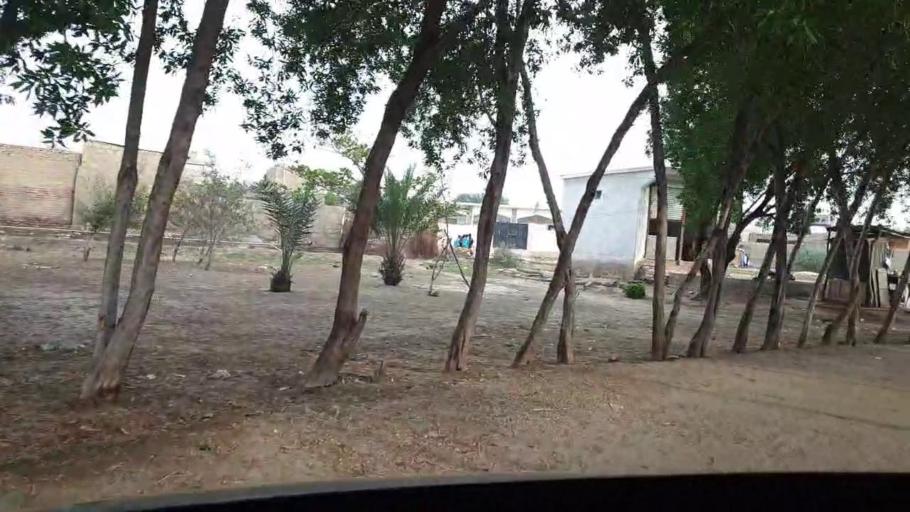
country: PK
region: Sindh
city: Thatta
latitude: 24.5987
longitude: 68.0822
